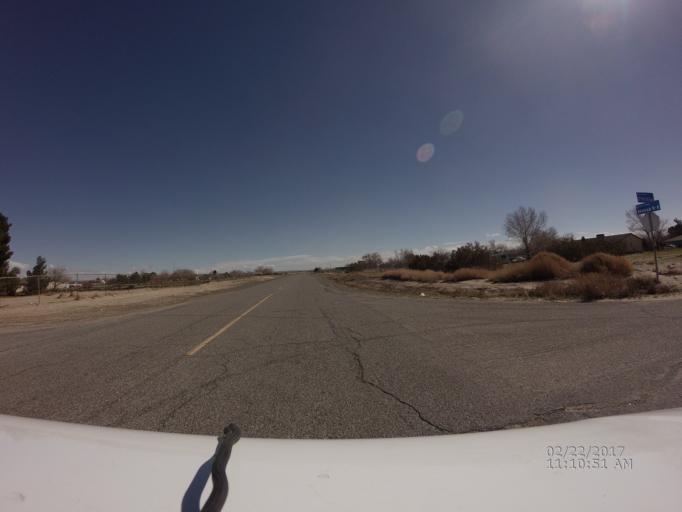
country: US
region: California
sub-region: Los Angeles County
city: Lake Los Angeles
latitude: 34.6239
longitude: -117.8137
